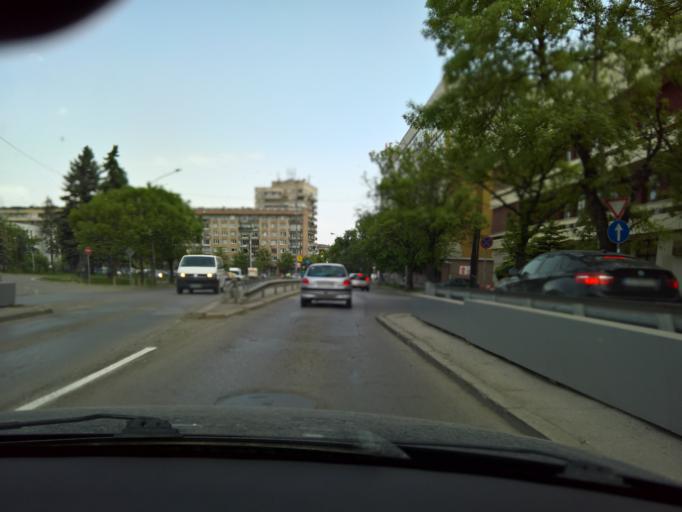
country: BG
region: Sofia-Capital
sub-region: Stolichna Obshtina
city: Sofia
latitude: 42.6803
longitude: 23.3565
